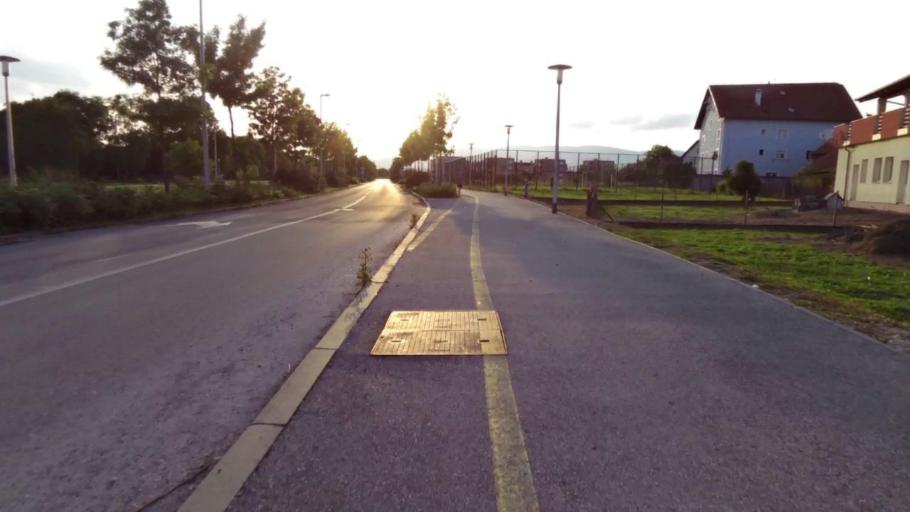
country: HR
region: Grad Zagreb
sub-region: Sesvete
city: Sesvete
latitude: 45.8319
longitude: 16.0937
